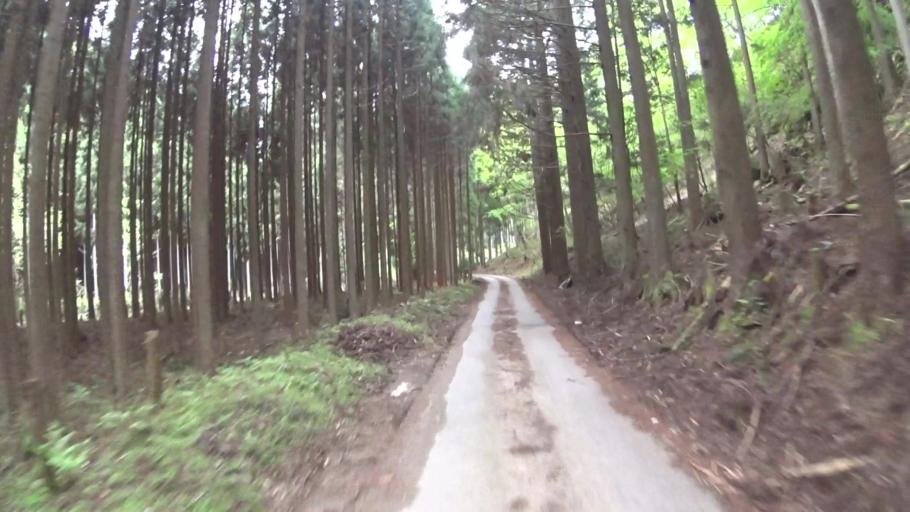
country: JP
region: Kyoto
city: Kameoka
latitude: 35.1135
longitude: 135.6320
